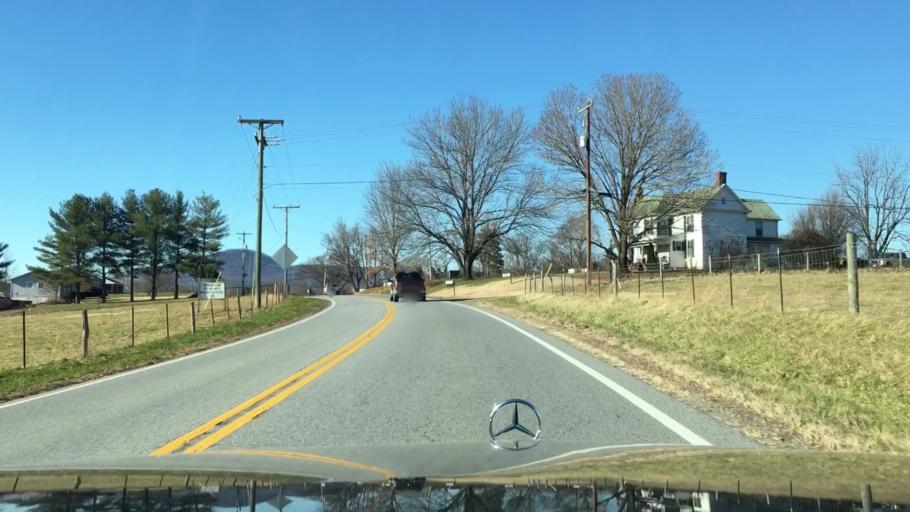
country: US
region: Virginia
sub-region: Botetourt County
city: Blue Ridge
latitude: 37.2673
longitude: -79.7592
